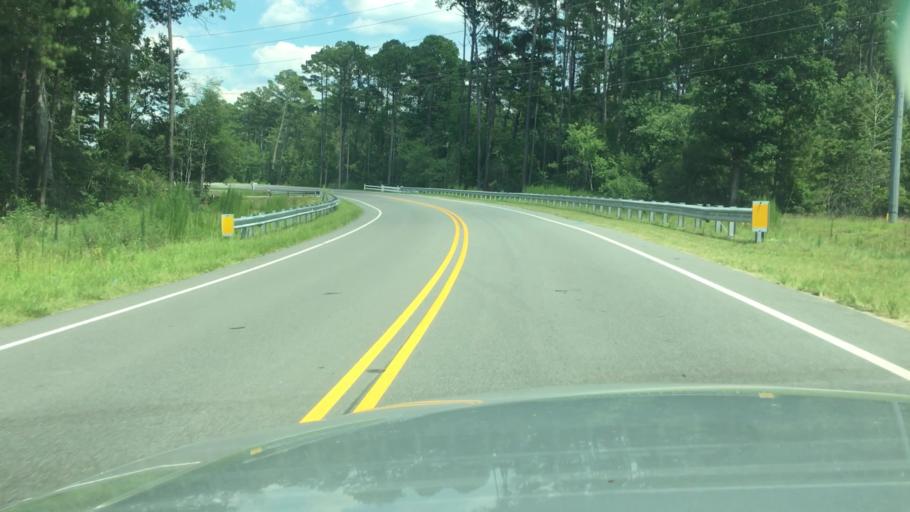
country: US
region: North Carolina
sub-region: Cumberland County
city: Hope Mills
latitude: 34.9470
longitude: -78.8821
